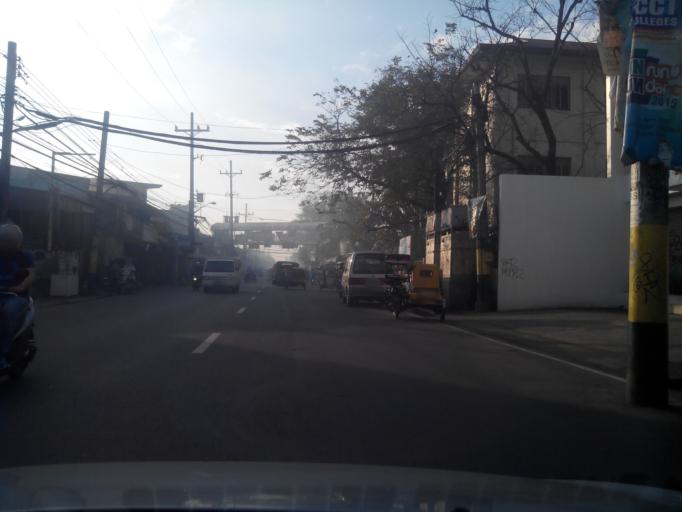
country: PH
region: Calabarzon
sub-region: Province of Rizal
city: Taytay
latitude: 14.5638
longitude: 121.1330
